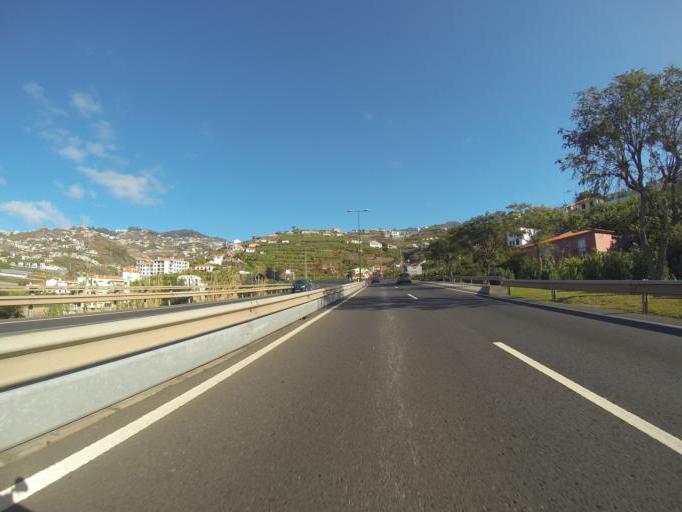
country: PT
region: Madeira
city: Camara de Lobos
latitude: 32.6592
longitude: -16.9755
